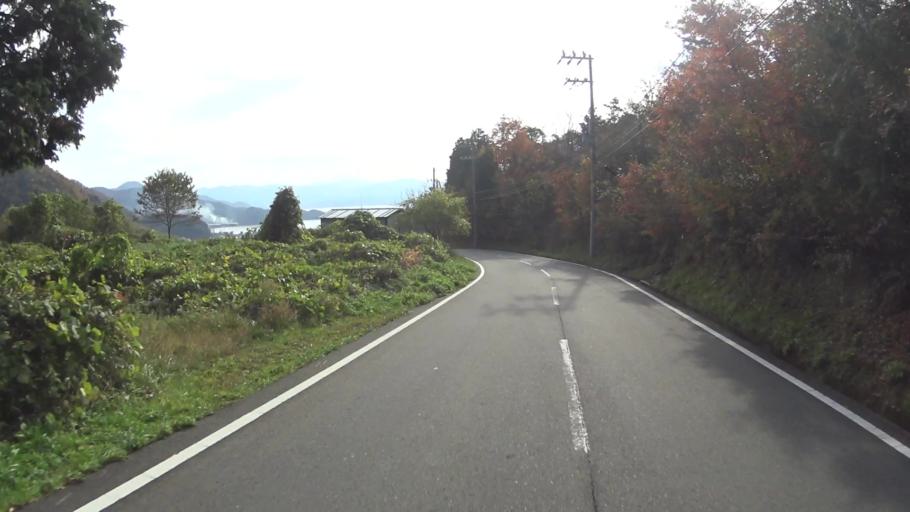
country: JP
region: Kyoto
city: Maizuru
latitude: 35.5302
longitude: 135.3927
